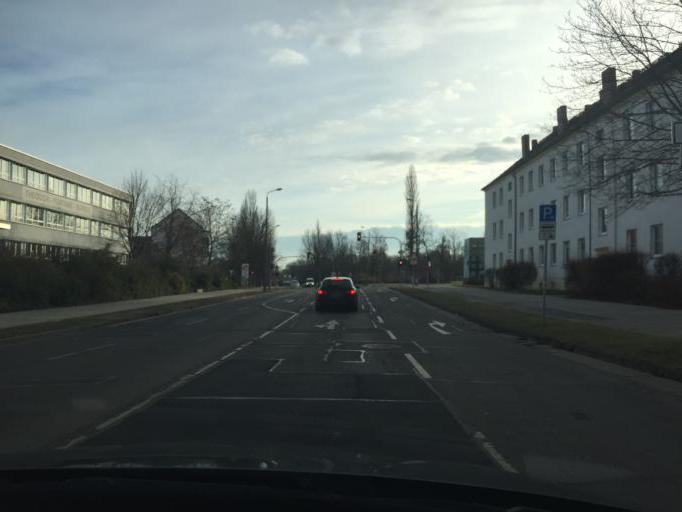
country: DE
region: Brandenburg
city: Cottbus
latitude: 51.7571
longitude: 14.3462
